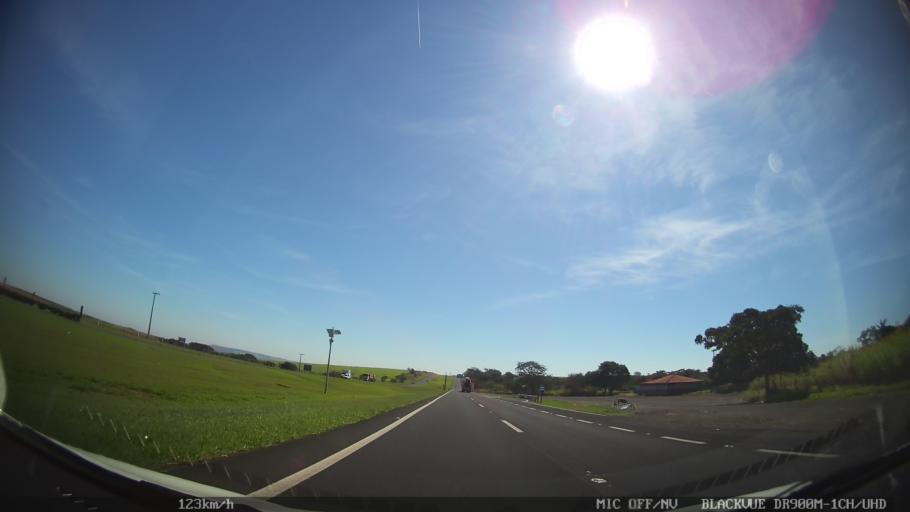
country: BR
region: Sao Paulo
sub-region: Santa Rita Do Passa Quatro
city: Santa Rita do Passa Quatro
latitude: -21.6780
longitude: -47.6040
